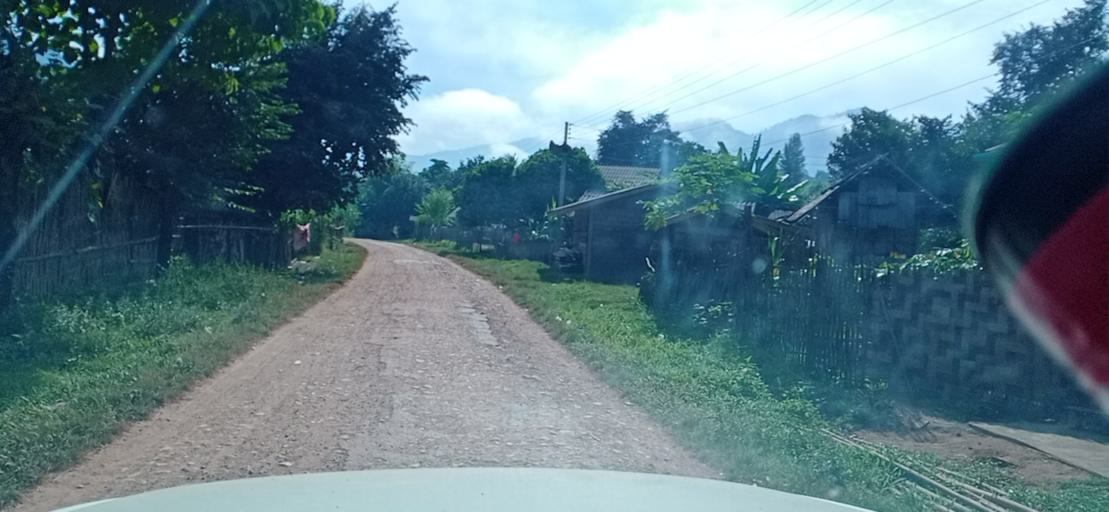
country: TH
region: Changwat Bueng Kan
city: Pak Khat
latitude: 18.6765
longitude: 103.1934
